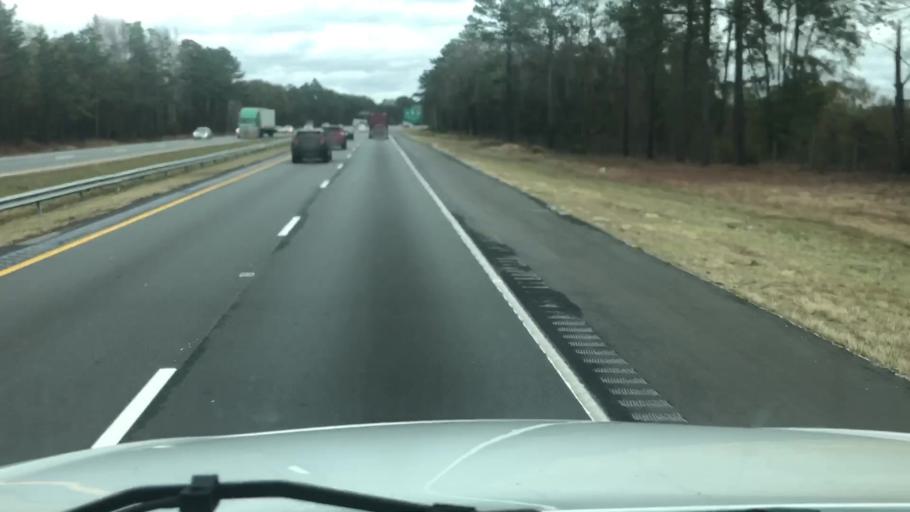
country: US
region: North Carolina
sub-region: Cumberland County
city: Eastover
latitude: 35.1079
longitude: -78.7689
